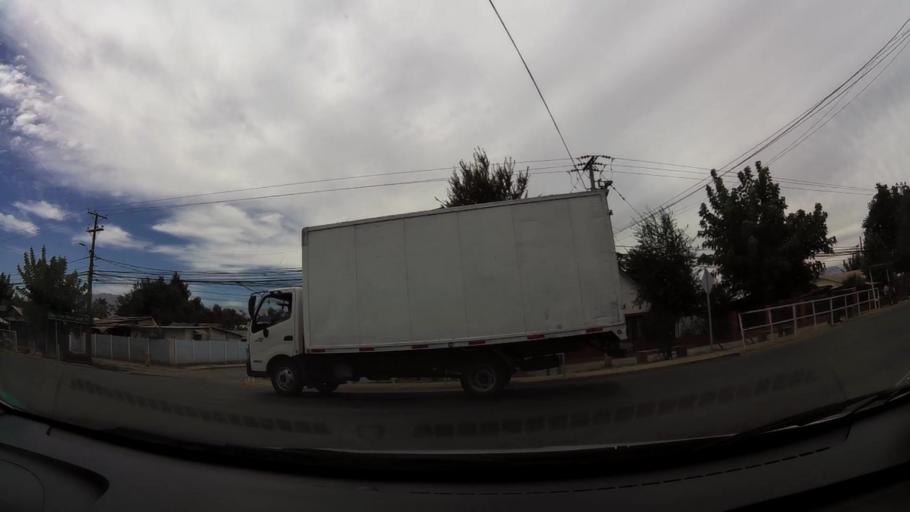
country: CL
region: O'Higgins
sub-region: Provincia de Cachapoal
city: Graneros
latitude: -34.0767
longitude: -70.7347
